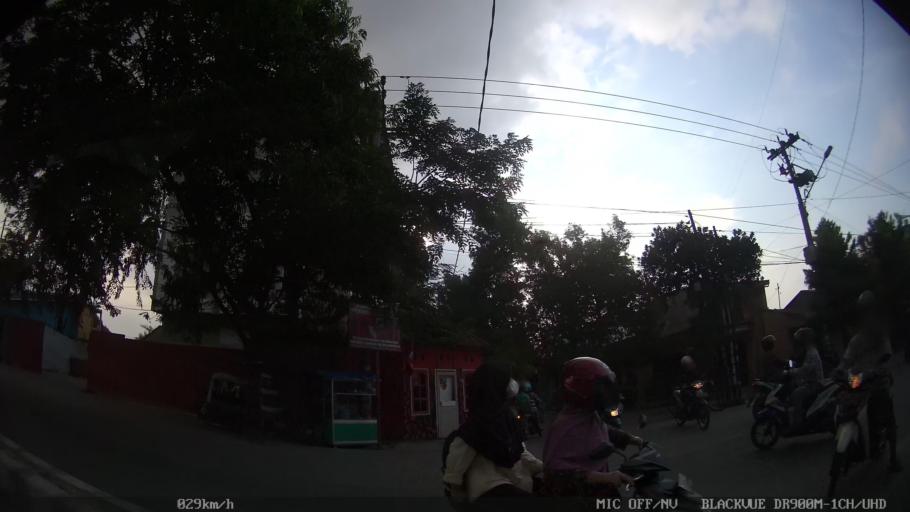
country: ID
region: North Sumatra
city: Medan
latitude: 3.5854
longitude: 98.7112
